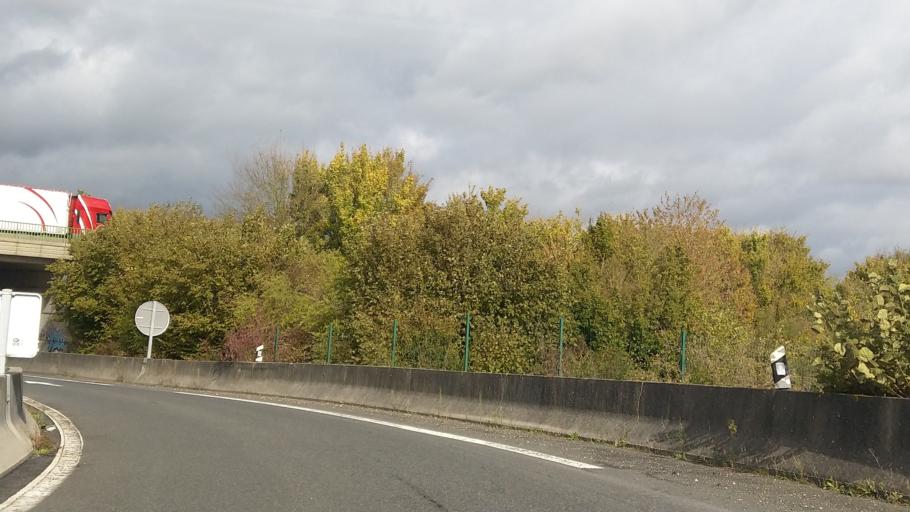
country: FR
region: Ile-de-France
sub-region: Departement du Val-d'Oise
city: Belloy-en-France
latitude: 49.0676
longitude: 2.3862
